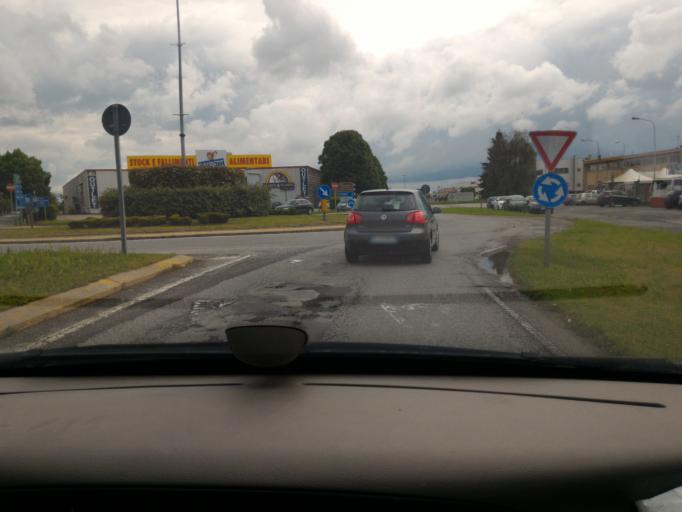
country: IT
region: Piedmont
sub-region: Provincia di Cuneo
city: Genola
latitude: 44.5956
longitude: 7.6590
